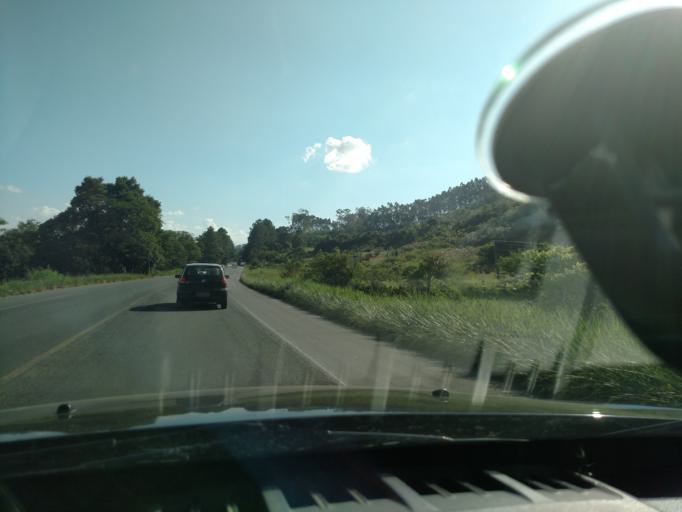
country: BR
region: Santa Catarina
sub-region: Rio Do Sul
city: Rio do Sul
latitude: -27.2714
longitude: -49.7329
